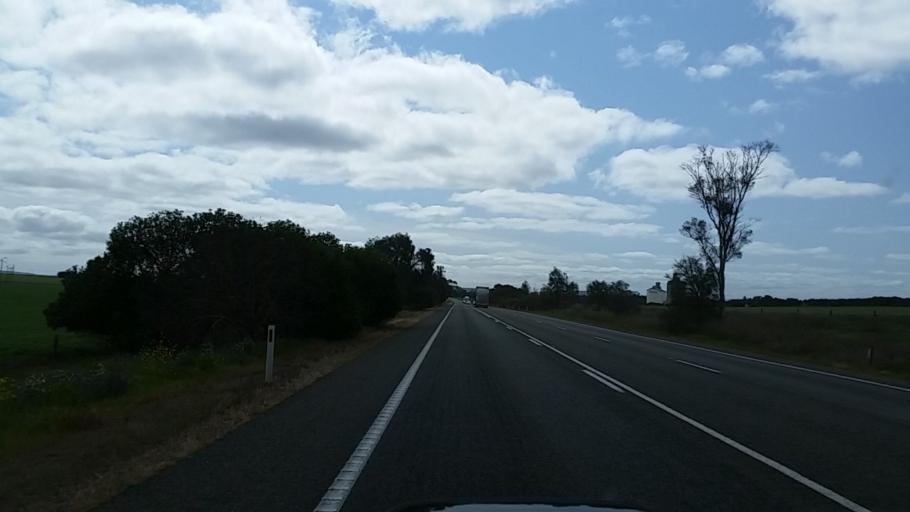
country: AU
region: South Australia
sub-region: Port Pirie City and Dists
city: Crystal Brook
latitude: -33.5546
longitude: 138.2218
